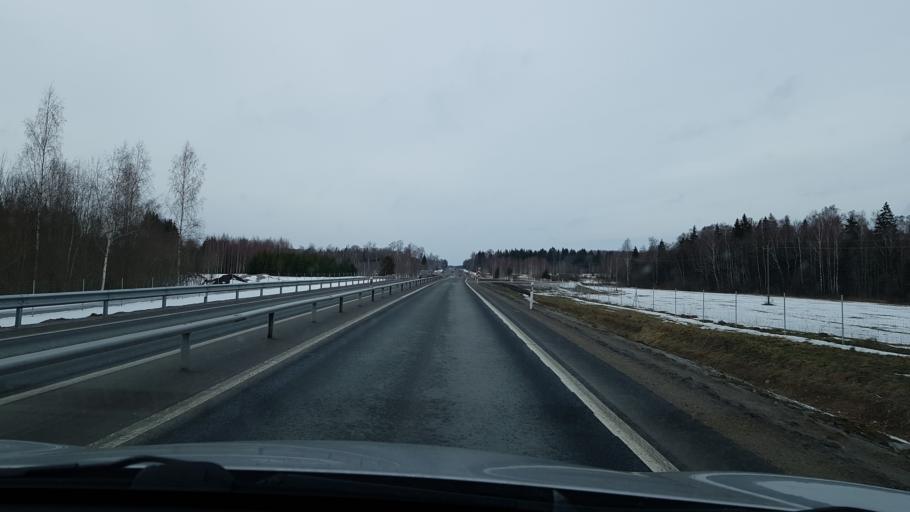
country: EE
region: Tartu
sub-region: Puhja vald
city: Puhja
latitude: 58.4487
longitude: 26.4292
